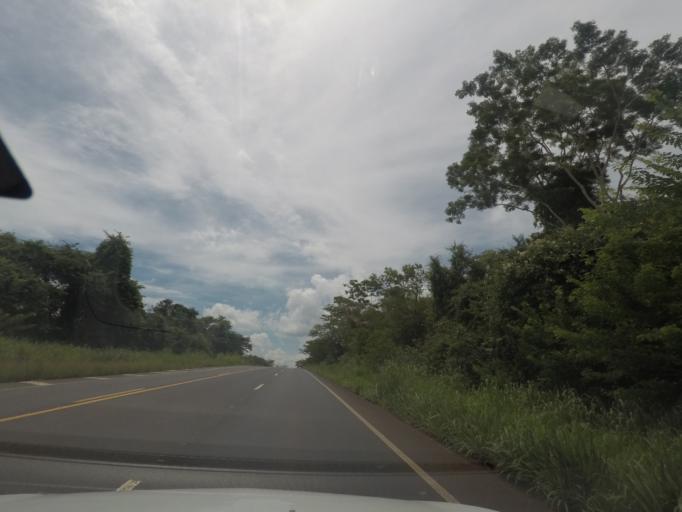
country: BR
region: Sao Paulo
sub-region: Barretos
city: Barretos
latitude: -20.4213
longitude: -48.6305
